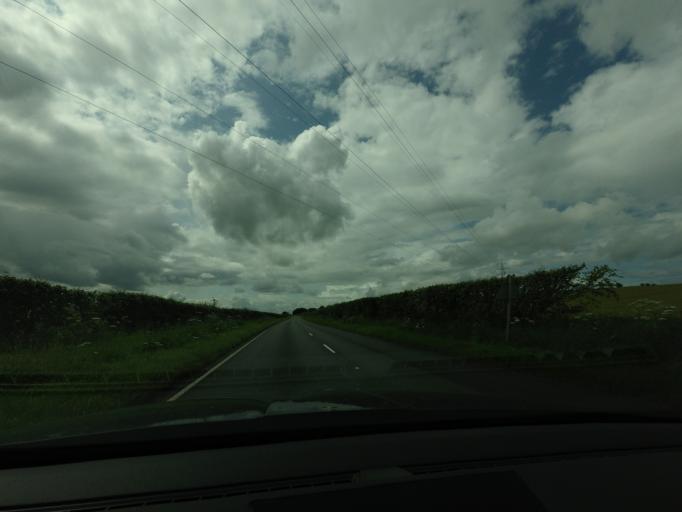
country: GB
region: Scotland
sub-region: Aberdeenshire
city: Whitehills
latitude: 57.6572
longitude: -2.6041
